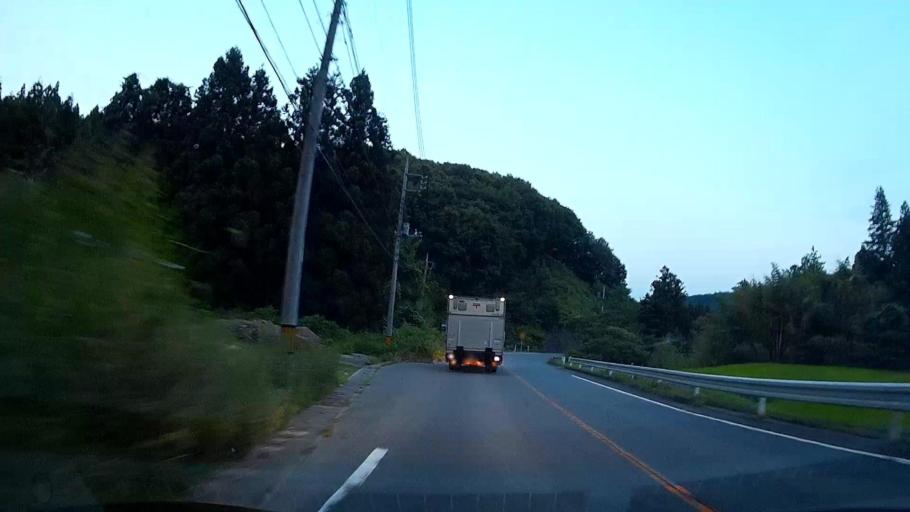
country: JP
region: Gunma
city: Annaka
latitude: 36.3872
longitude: 138.8568
